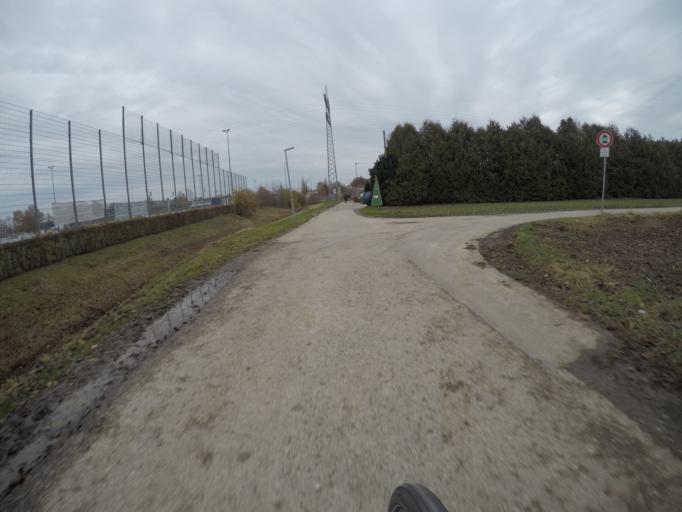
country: DE
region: Baden-Wuerttemberg
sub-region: Regierungsbezirk Stuttgart
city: Leinfelden-Echterdingen
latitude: 48.6886
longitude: 9.1517
